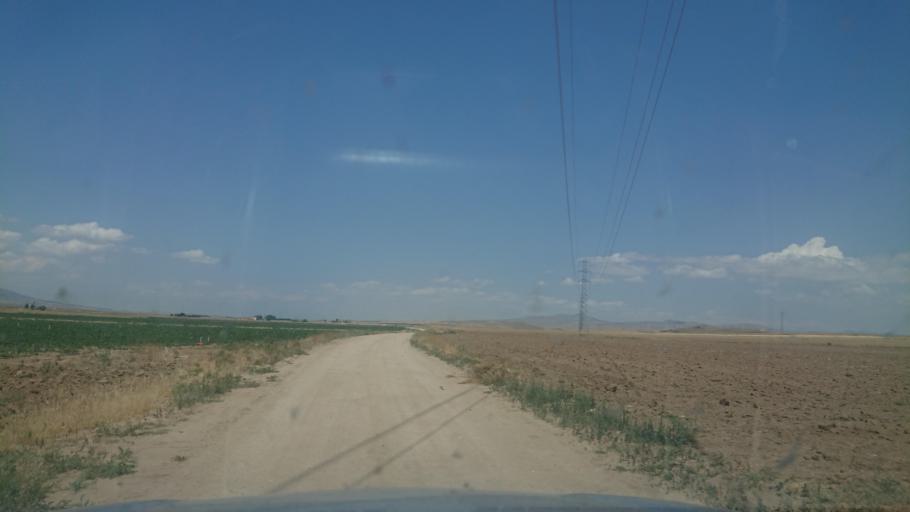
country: TR
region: Aksaray
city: Sariyahsi
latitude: 39.0107
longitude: 33.8799
